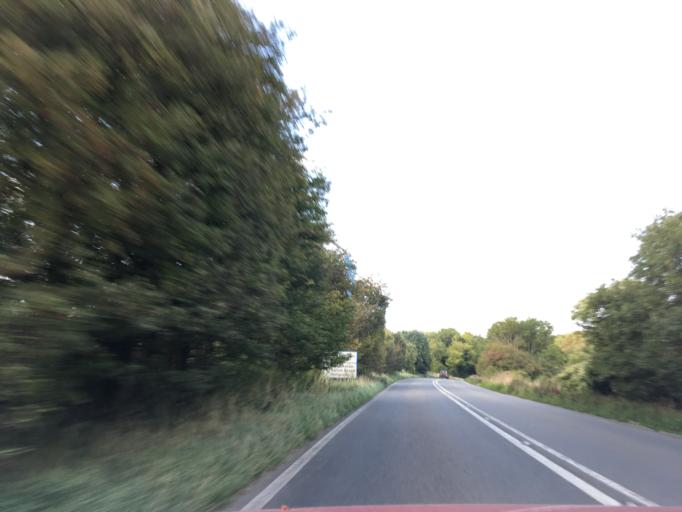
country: GB
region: England
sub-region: Gloucestershire
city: Bourton on the Water
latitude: 51.8650
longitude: -1.7974
